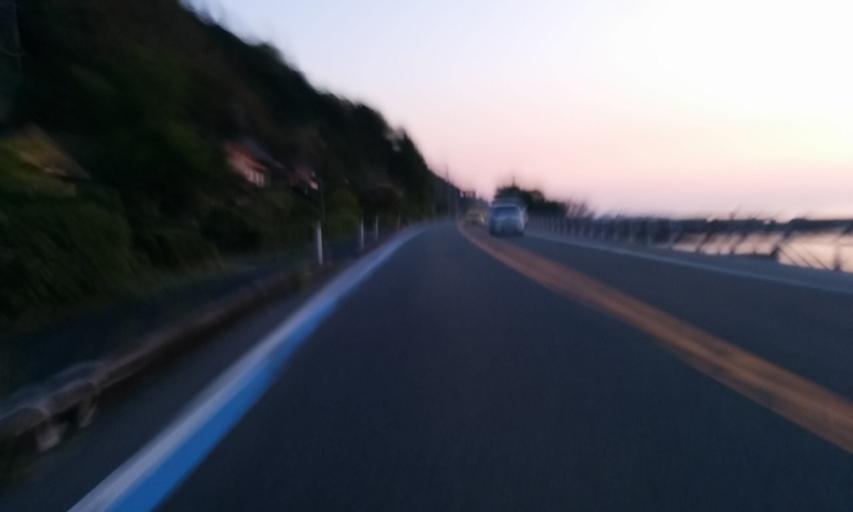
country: JP
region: Ehime
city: Ozu
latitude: 33.6363
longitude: 132.5294
